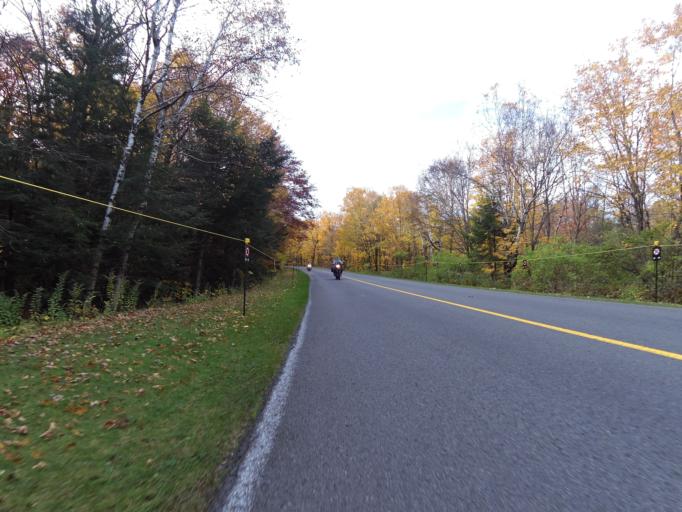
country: CA
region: Quebec
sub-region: Outaouais
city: Gatineau
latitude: 45.4807
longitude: -75.8497
